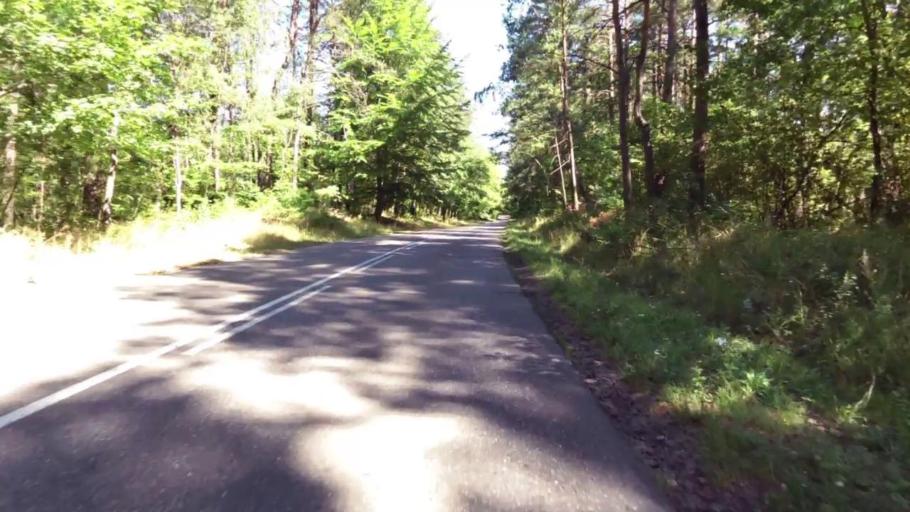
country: PL
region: West Pomeranian Voivodeship
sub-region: Powiat szczecinecki
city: Borne Sulinowo
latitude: 53.5819
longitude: 16.5702
